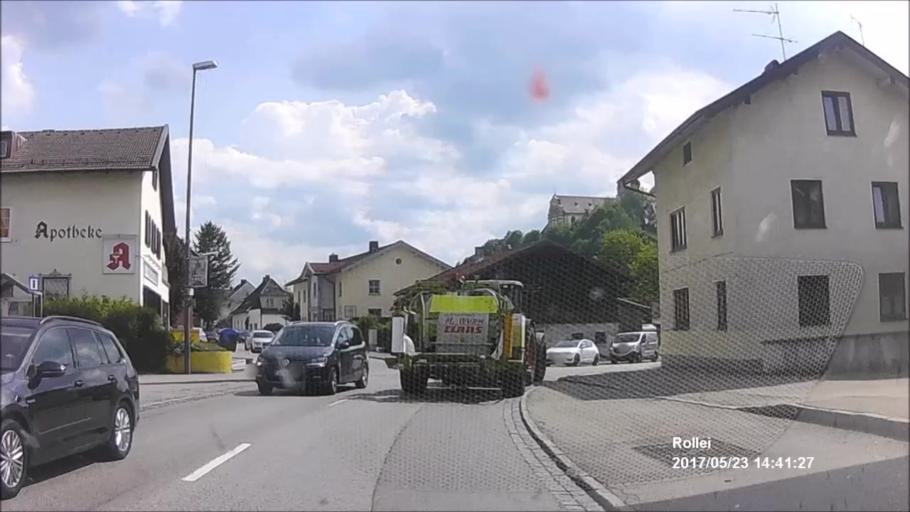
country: DE
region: Bavaria
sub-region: Upper Bavaria
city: Trostberg an der Alz
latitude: 48.0026
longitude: 12.5357
